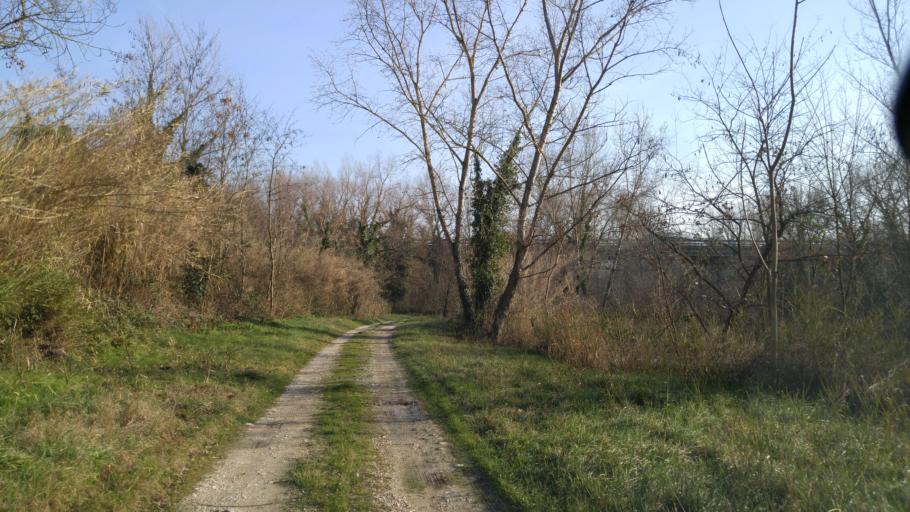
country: IT
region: The Marches
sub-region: Provincia di Pesaro e Urbino
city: Tavernelle
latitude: 43.7334
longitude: 12.8970
